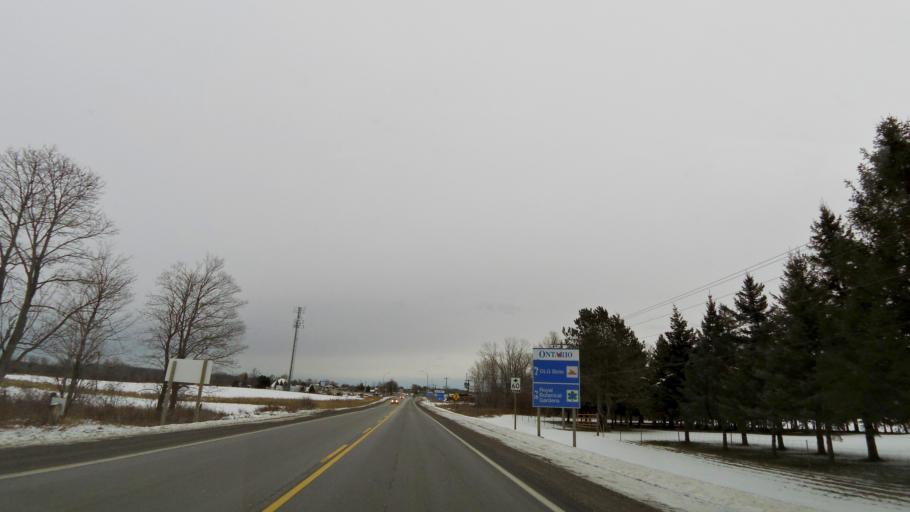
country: CA
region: Ontario
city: Ancaster
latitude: 43.2836
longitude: -80.0747
